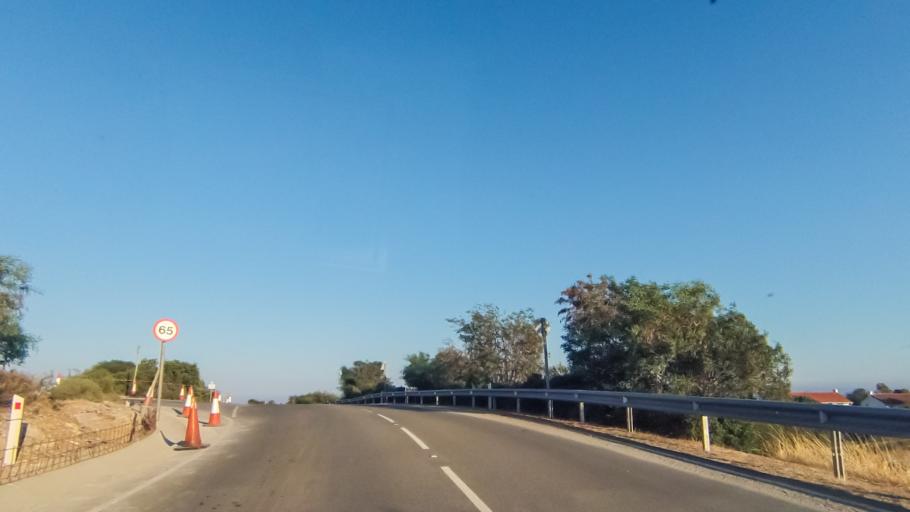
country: CY
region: Limassol
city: Sotira
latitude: 34.6746
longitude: 32.8096
